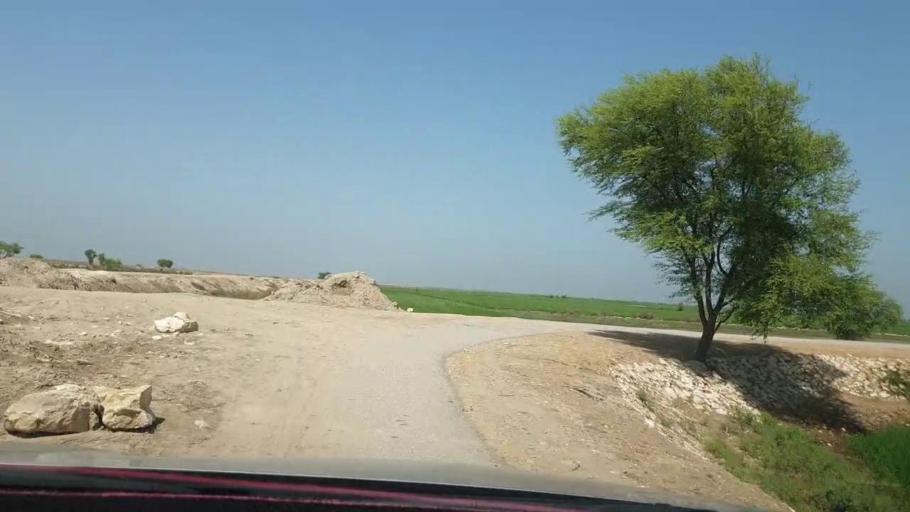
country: PK
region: Sindh
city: Warah
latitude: 27.5616
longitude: 67.7408
